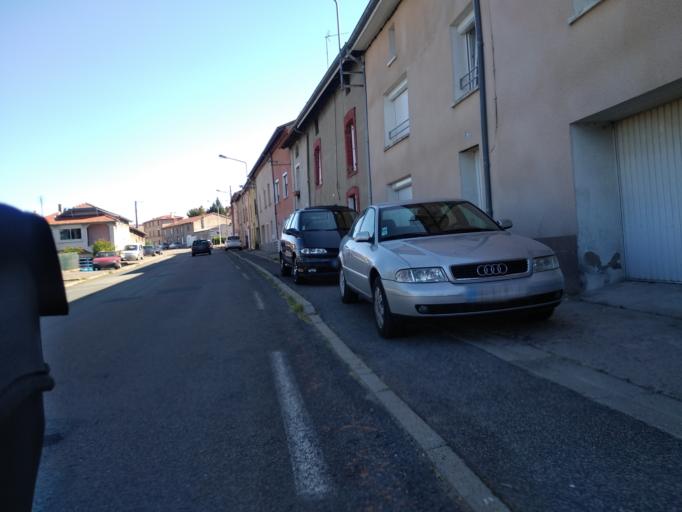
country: FR
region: Rhone-Alpes
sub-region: Departement de la Loire
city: Neulise
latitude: 45.8963
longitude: 4.1815
